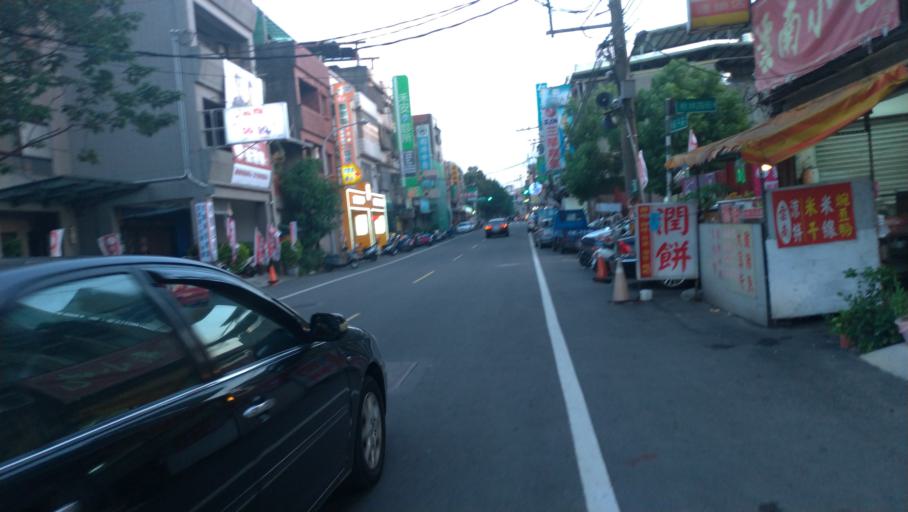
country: TW
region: Taiwan
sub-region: Taoyuan
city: Taoyuan
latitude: 24.9847
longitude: 121.3145
